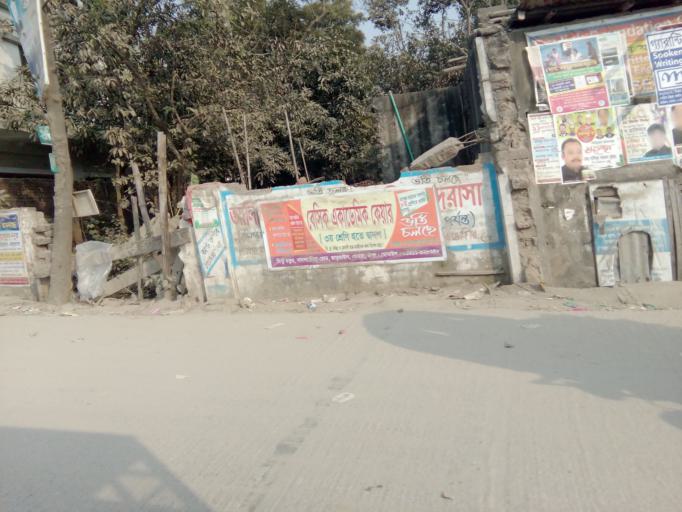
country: BD
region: Dhaka
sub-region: Dhaka
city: Dhaka
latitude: 23.6942
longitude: 90.4756
